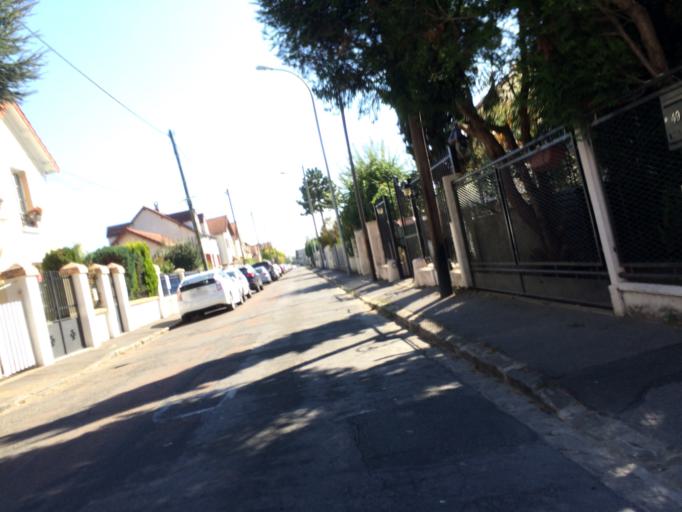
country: FR
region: Ile-de-France
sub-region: Departement de l'Essonne
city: Savigny-sur-Orge
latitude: 48.6876
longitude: 2.3609
